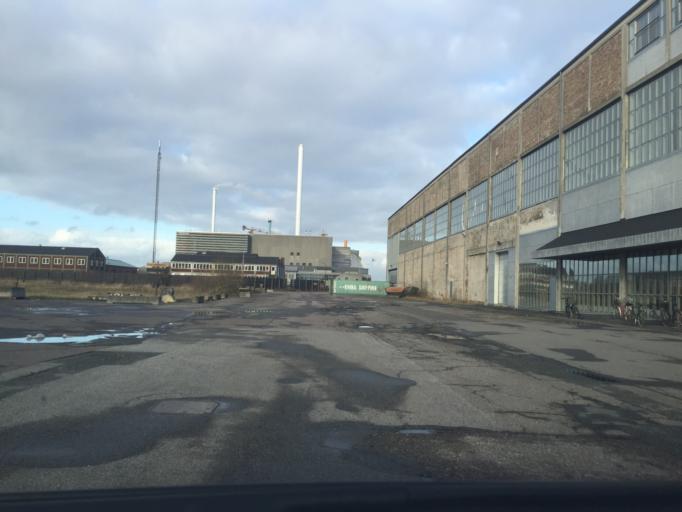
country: DK
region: Capital Region
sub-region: Kobenhavn
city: Christianshavn
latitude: 55.6935
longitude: 12.6132
